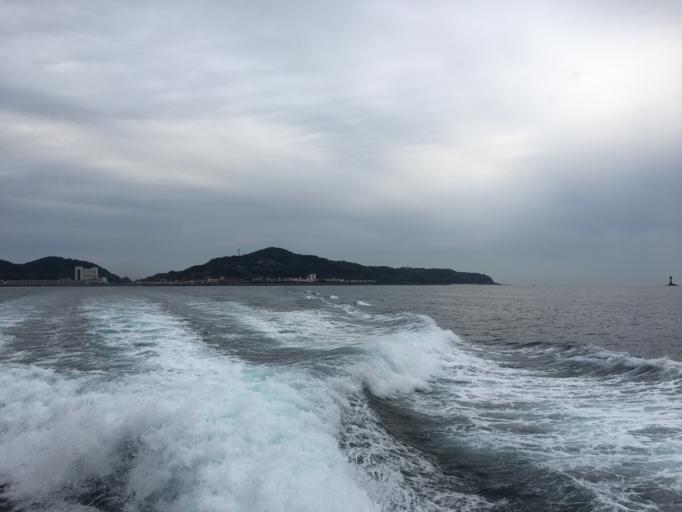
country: JP
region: Nagasaki
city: Nagasaki-shi
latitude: 32.7059
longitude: 129.7928
